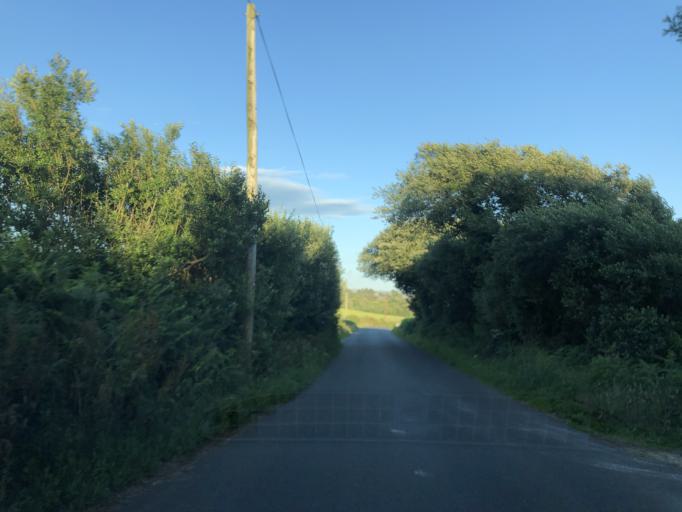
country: GB
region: England
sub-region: Isle of Wight
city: Chale
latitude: 50.6346
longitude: -1.3298
